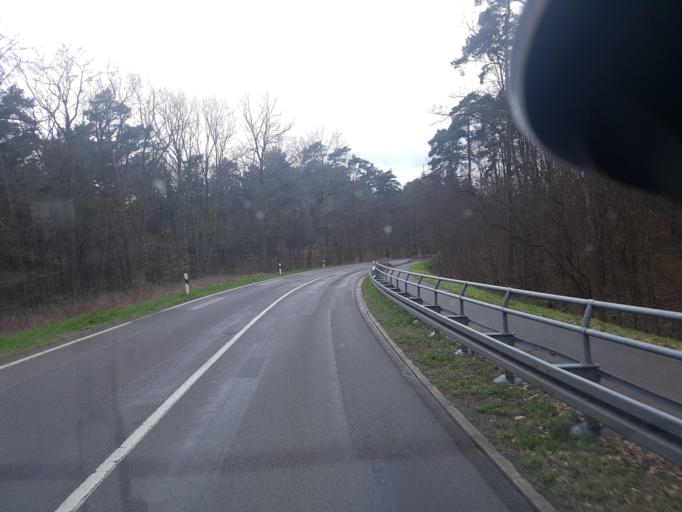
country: DE
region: Brandenburg
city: Mixdorf
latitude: 52.1370
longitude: 14.4693
